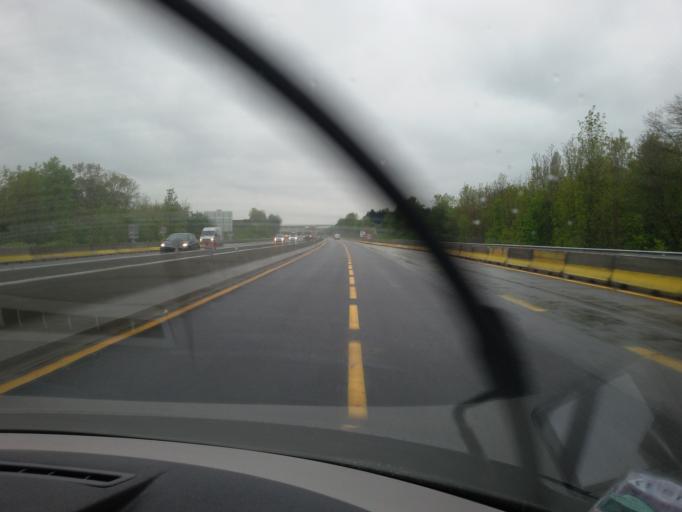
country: FR
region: Rhone-Alpes
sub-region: Departement du Rhone
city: Limonest
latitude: 45.8275
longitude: 4.7626
